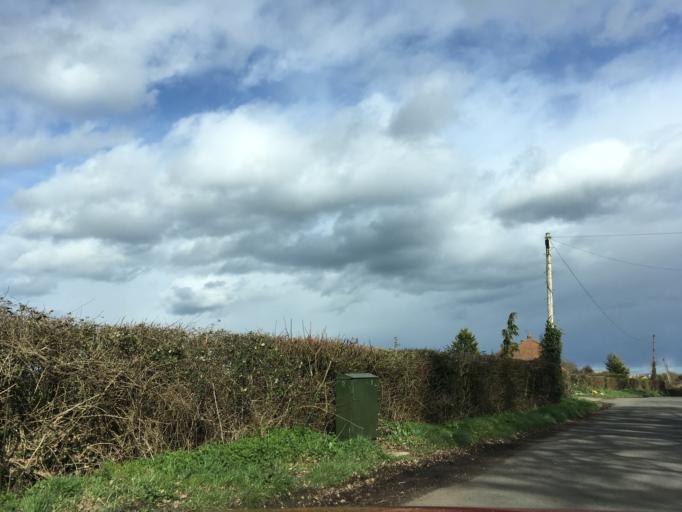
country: GB
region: England
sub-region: Gloucestershire
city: Newent
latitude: 51.8445
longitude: -2.4005
